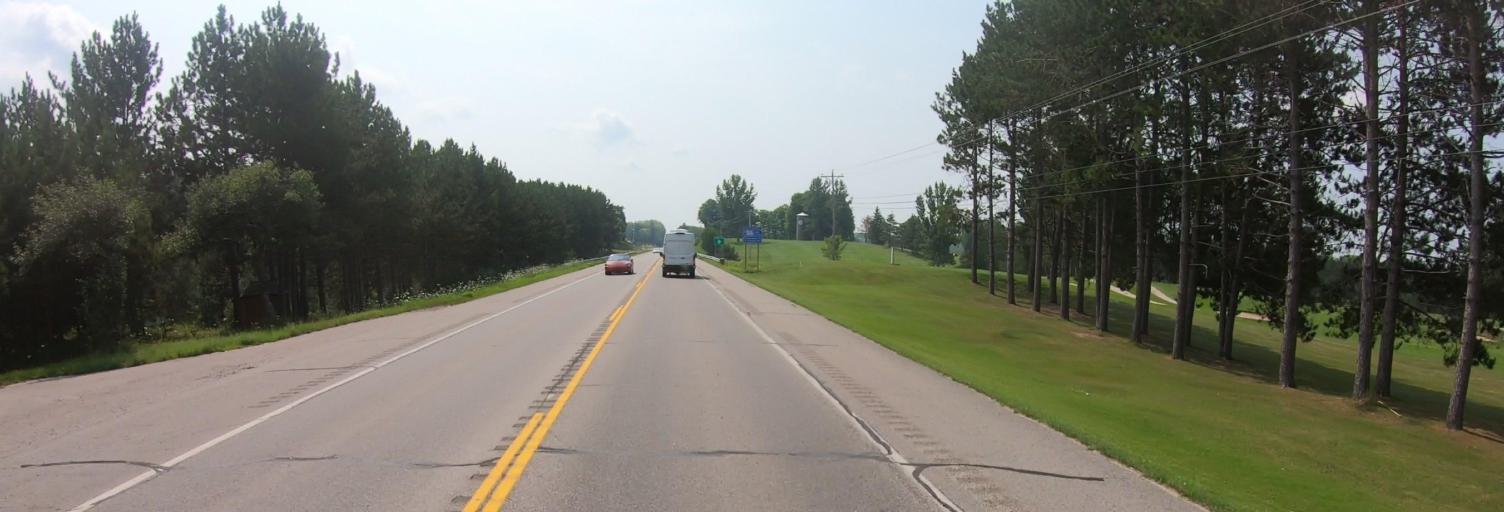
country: US
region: Michigan
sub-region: Luce County
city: Newberry
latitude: 46.3085
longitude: -85.5096
